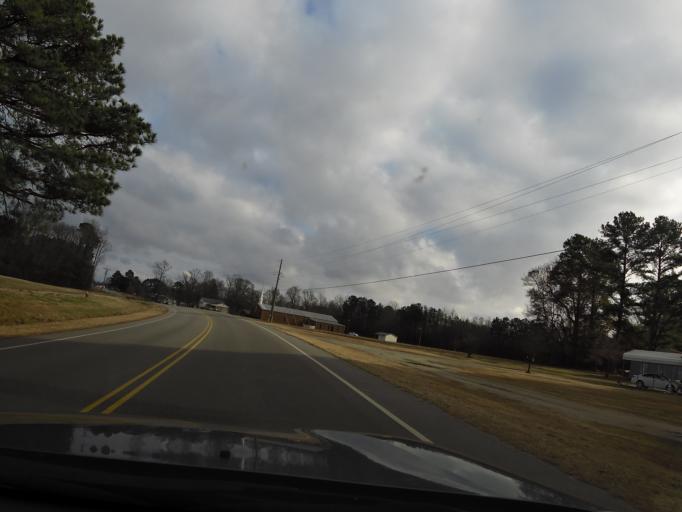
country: US
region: North Carolina
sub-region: Edgecombe County
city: Pinetops
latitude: 35.8131
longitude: -77.6580
